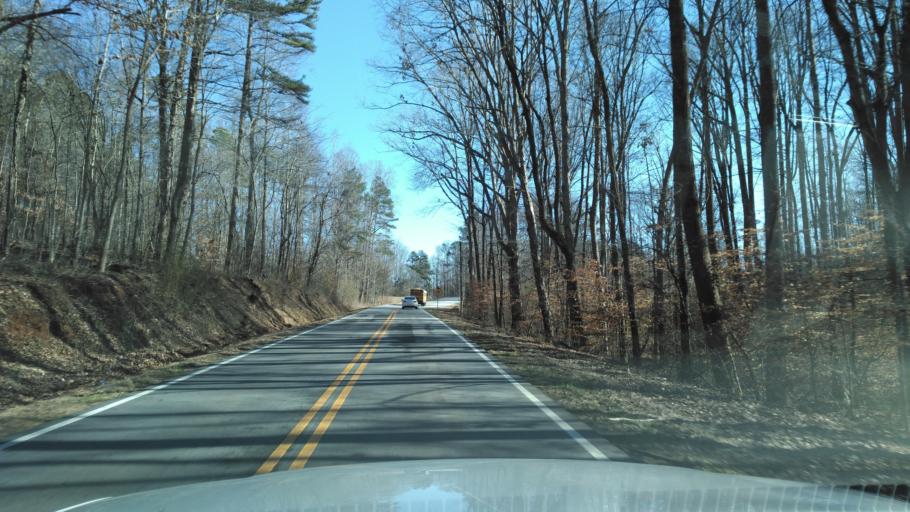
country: US
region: Georgia
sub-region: Hall County
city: Gainesville
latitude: 34.3114
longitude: -83.7430
